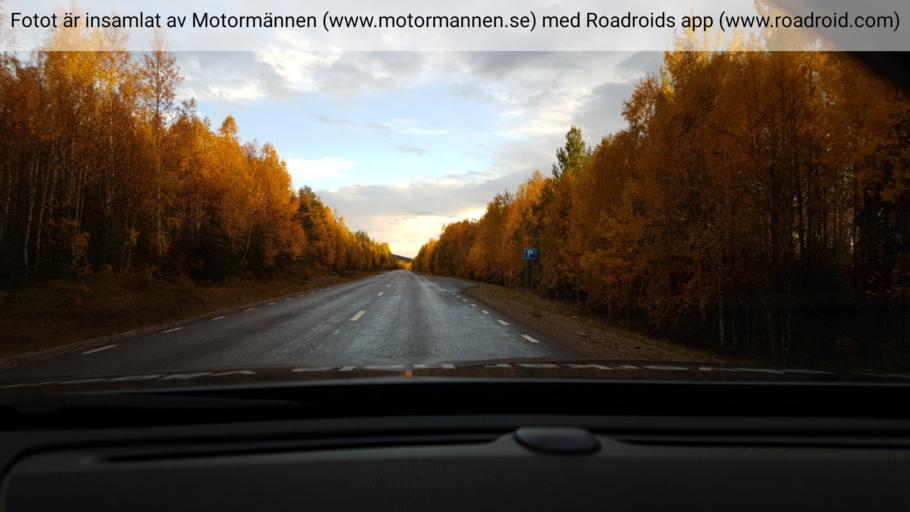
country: SE
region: Norrbotten
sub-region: Overkalix Kommun
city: OEverkalix
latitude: 66.5875
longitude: 22.7562
